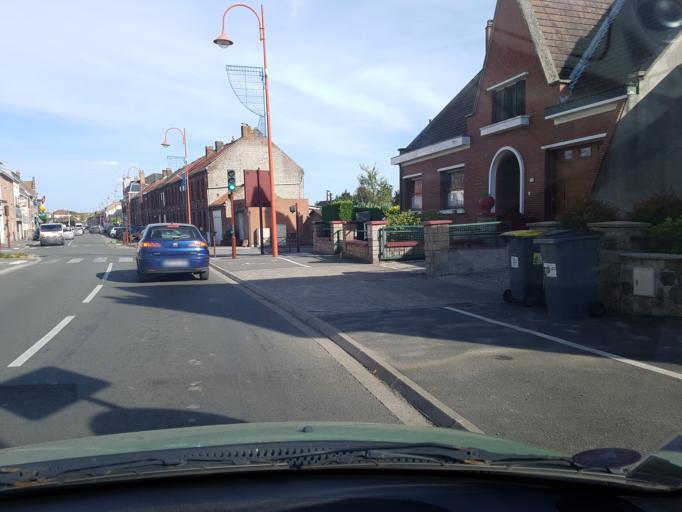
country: FR
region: Nord-Pas-de-Calais
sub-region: Departement du Pas-de-Calais
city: Annezin
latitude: 50.5393
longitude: 2.6210
